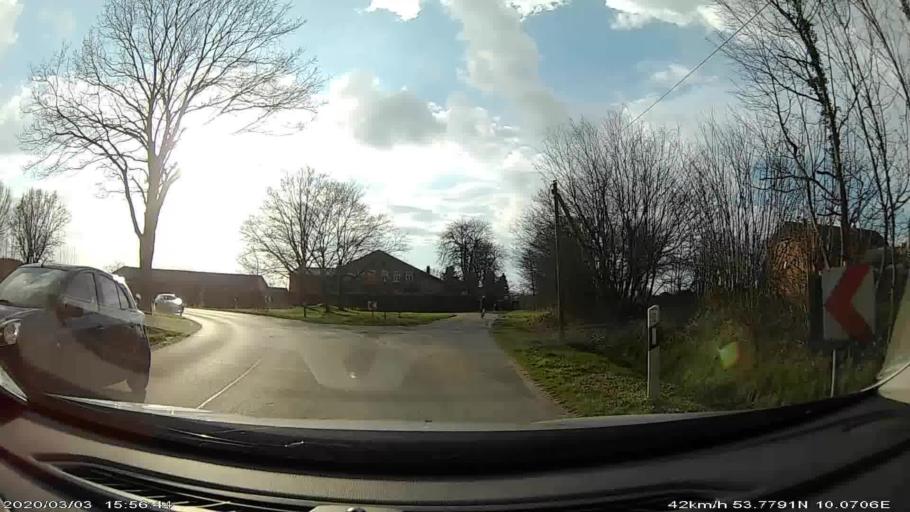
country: DE
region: Schleswig-Holstein
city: Tangstedt
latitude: 53.7792
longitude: 10.0724
